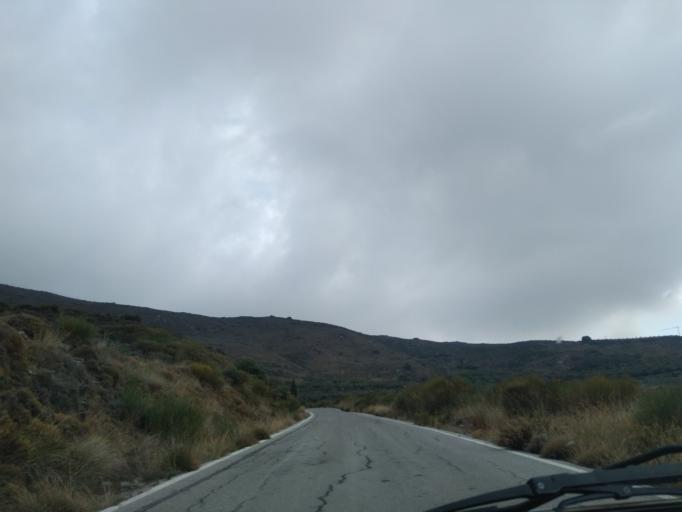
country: GR
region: Crete
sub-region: Nomos Lasithiou
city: Siteia
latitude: 35.1444
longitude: 26.0232
